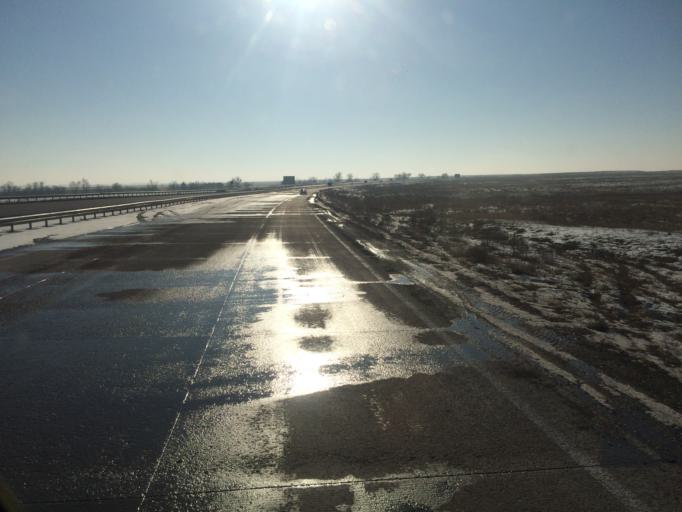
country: KG
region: Chuy
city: Kara-Balta
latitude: 43.1858
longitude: 73.9410
